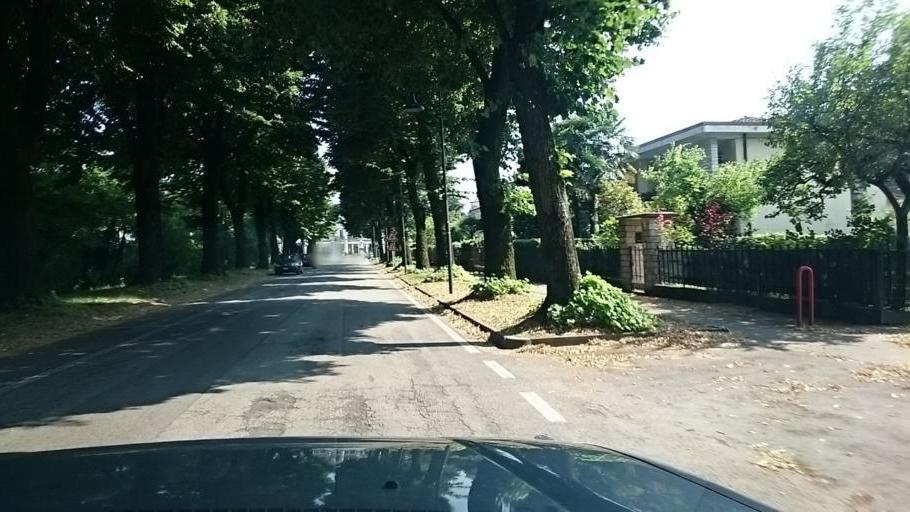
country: IT
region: Veneto
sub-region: Provincia di Padova
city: Galliera Veneta
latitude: 45.6651
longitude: 11.8316
